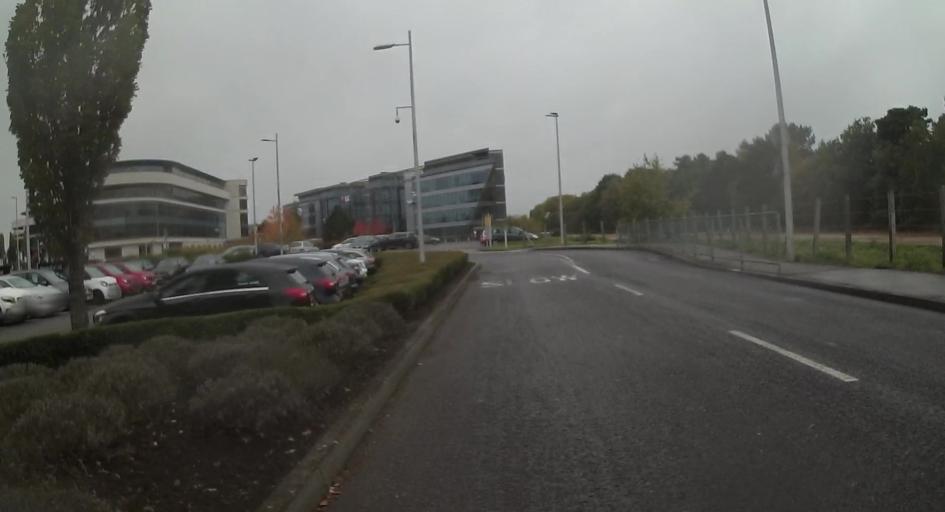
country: GB
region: England
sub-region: Surrey
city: Byfleet
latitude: 51.3545
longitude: -0.4698
